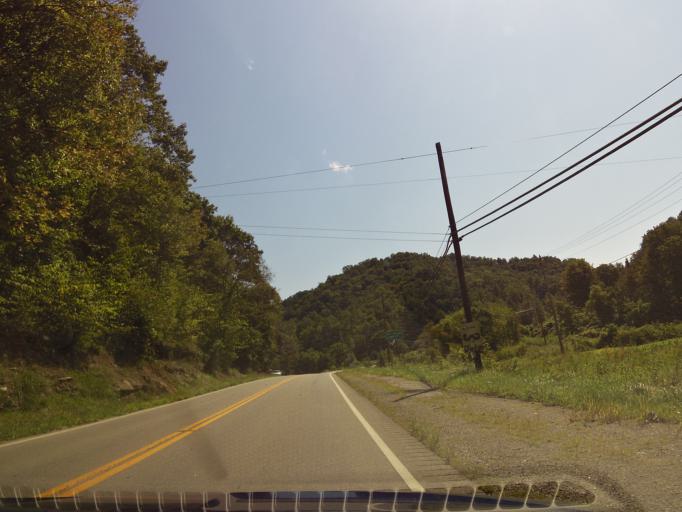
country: US
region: Kentucky
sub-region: Clay County
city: Manchester
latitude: 37.1159
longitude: -83.7232
